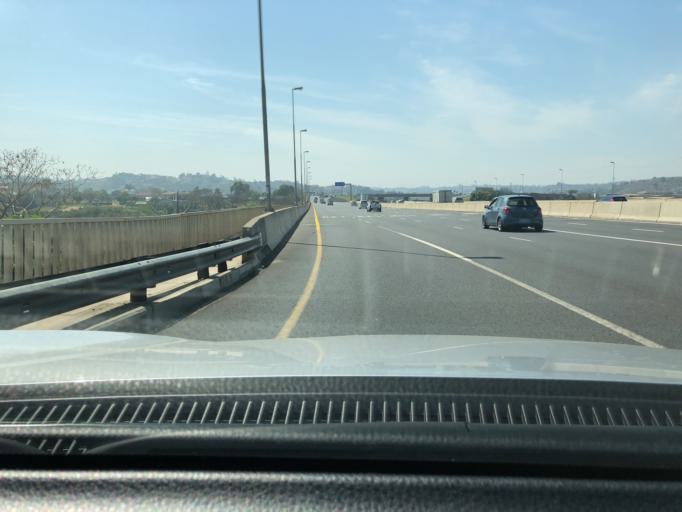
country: ZA
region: KwaZulu-Natal
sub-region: eThekwini Metropolitan Municipality
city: Berea
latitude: -29.8049
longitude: 30.9788
